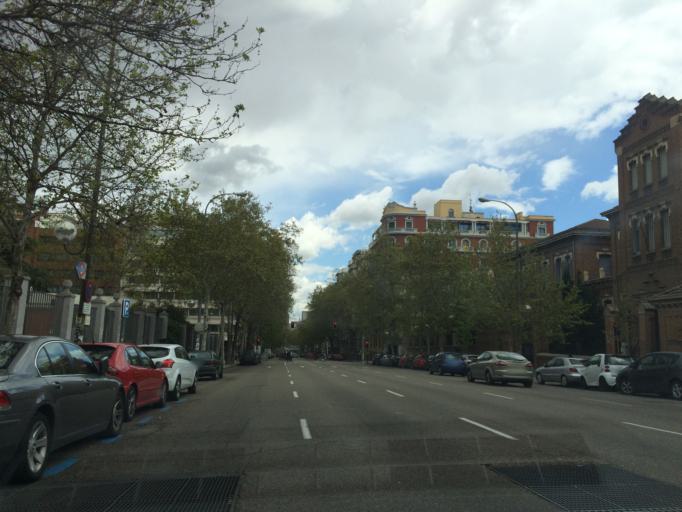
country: ES
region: Madrid
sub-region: Provincia de Madrid
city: Chamberi
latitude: 40.4384
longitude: -3.6976
